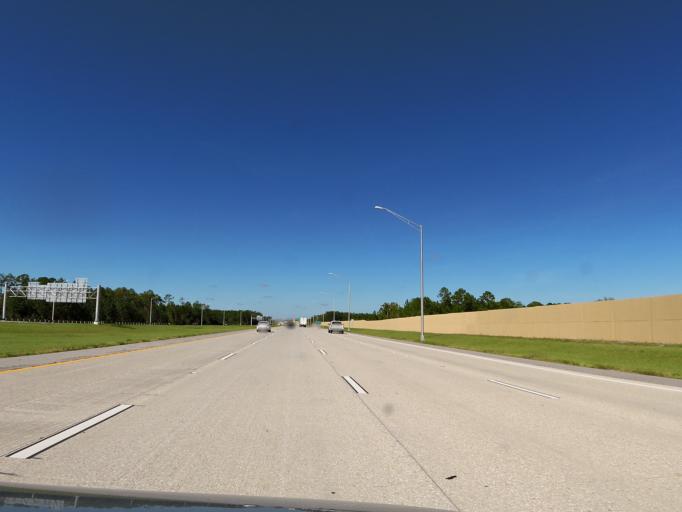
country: US
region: Florida
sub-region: Saint Johns County
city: Fruit Cove
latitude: 30.1203
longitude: -81.5120
